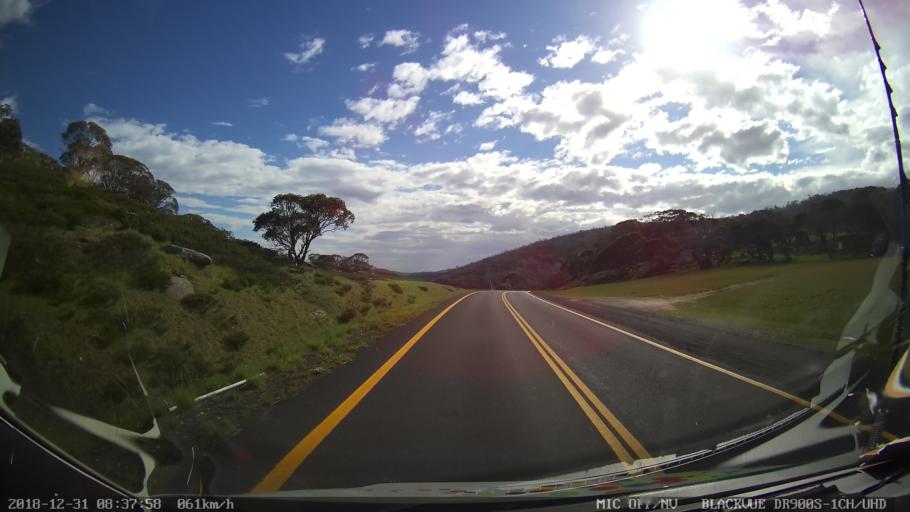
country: AU
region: New South Wales
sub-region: Snowy River
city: Jindabyne
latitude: -36.4165
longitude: 148.3903
